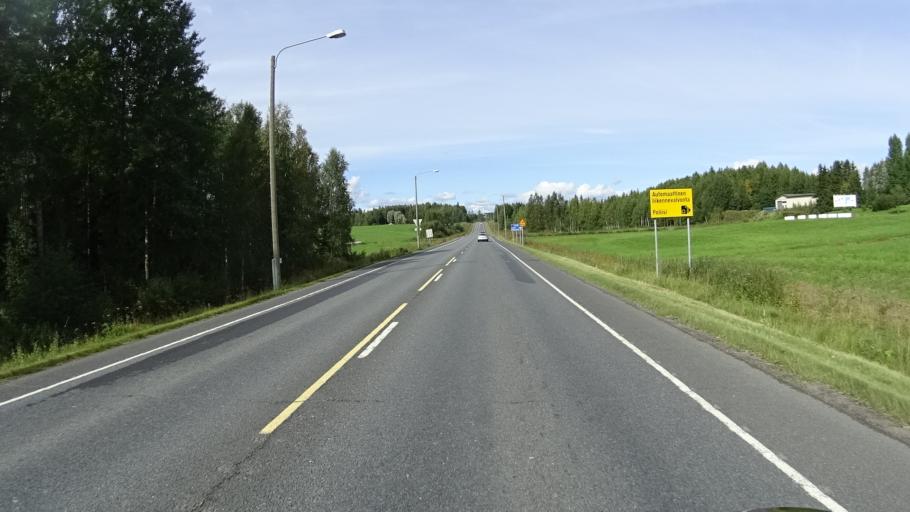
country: FI
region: Pirkanmaa
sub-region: Tampere
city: Haemeenkyroe
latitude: 61.6563
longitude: 23.1722
